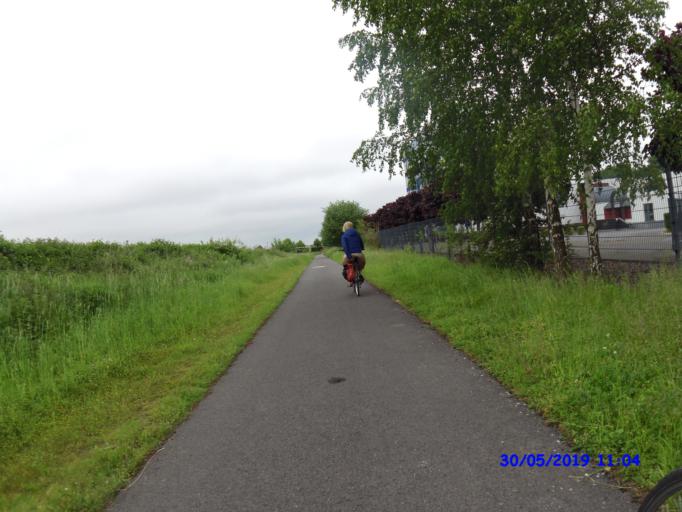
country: BE
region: Wallonia
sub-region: Province du Hainaut
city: Thuin
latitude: 50.2822
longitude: 4.3195
